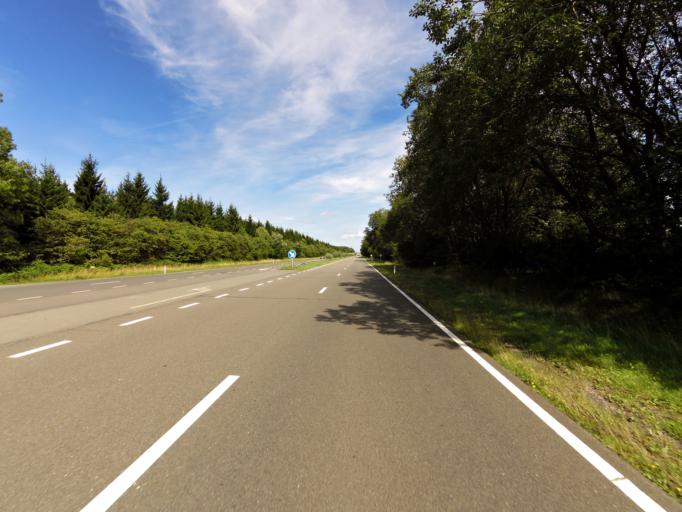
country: BE
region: Wallonia
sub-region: Province du Luxembourg
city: Tenneville
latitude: 50.0842
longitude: 5.4426
